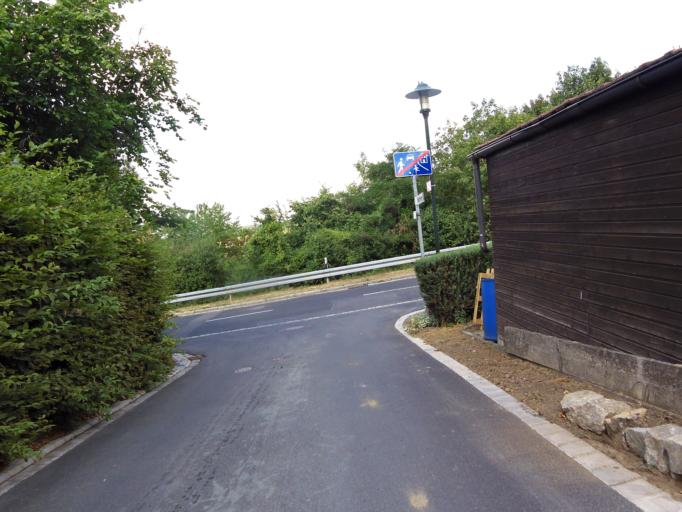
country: DE
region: Bavaria
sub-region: Regierungsbezirk Unterfranken
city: Gerbrunn
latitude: 49.7849
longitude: 10.0021
